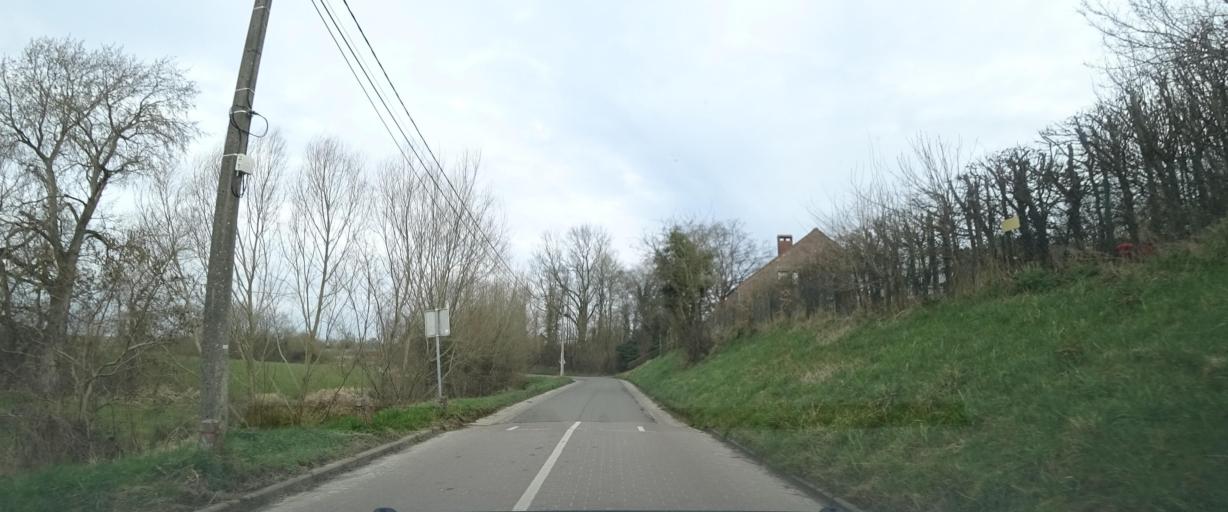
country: BE
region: Wallonia
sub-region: Province du Brabant Wallon
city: Chastre
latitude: 50.5925
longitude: 4.6051
